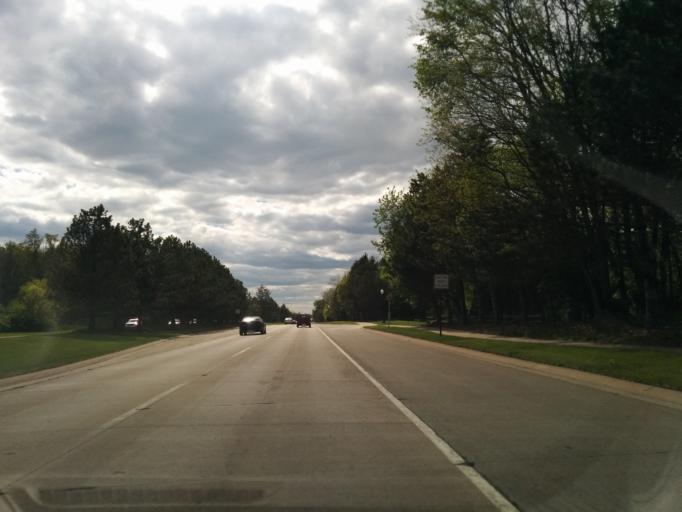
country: US
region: Michigan
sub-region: Oakland County
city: Farmington Hills
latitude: 42.4980
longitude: -83.4027
